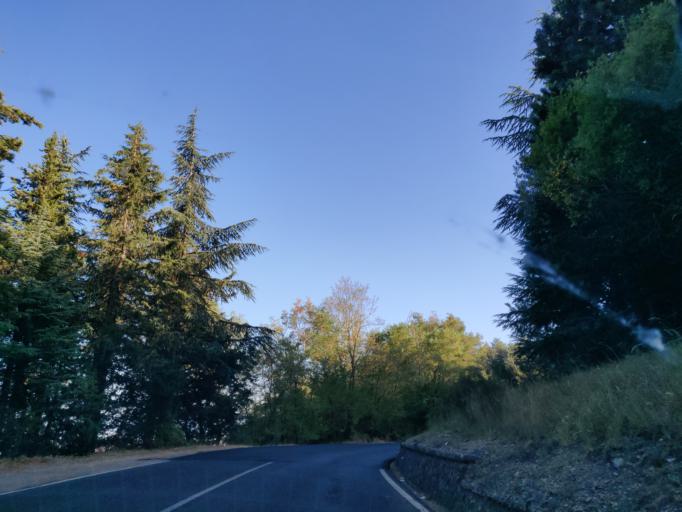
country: IT
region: Tuscany
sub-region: Provincia di Siena
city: Abbadia San Salvatore
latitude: 42.8728
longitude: 11.6836
